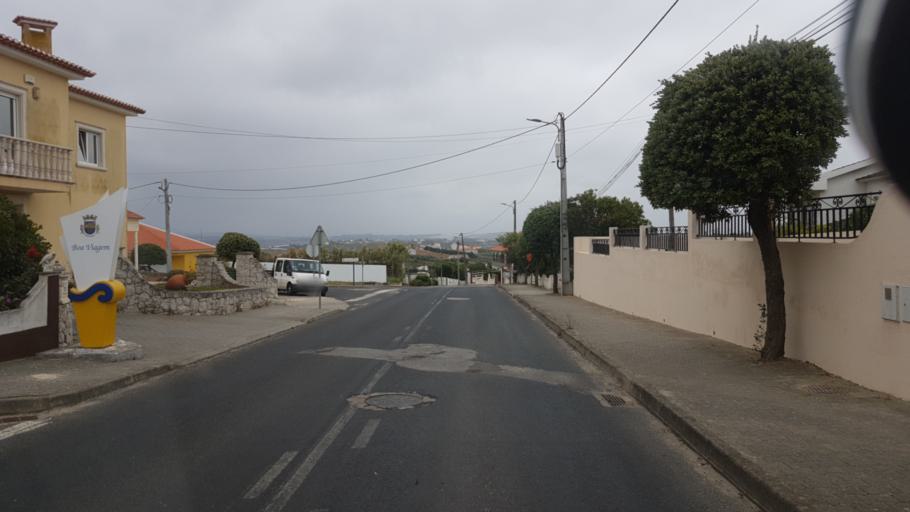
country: PT
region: Lisbon
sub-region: Lourinha
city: Lourinha
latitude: 39.1961
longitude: -9.3352
